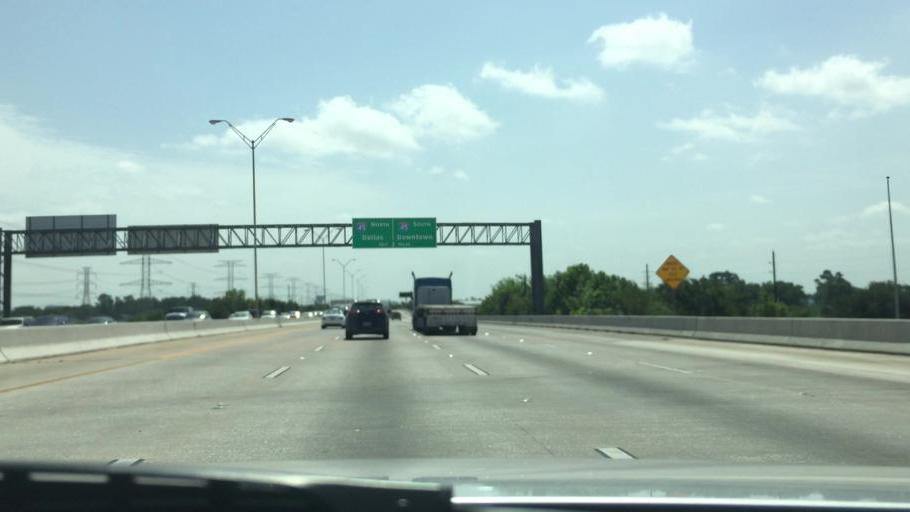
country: US
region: Texas
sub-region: Harris County
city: Hudson
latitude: 29.9375
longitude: -95.4597
